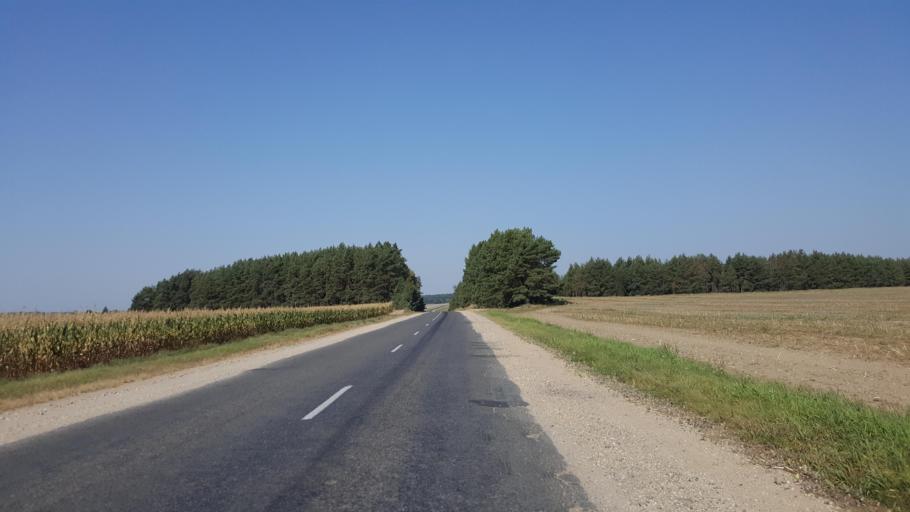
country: BY
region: Brest
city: Kamyanyets
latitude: 52.4079
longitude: 23.7389
